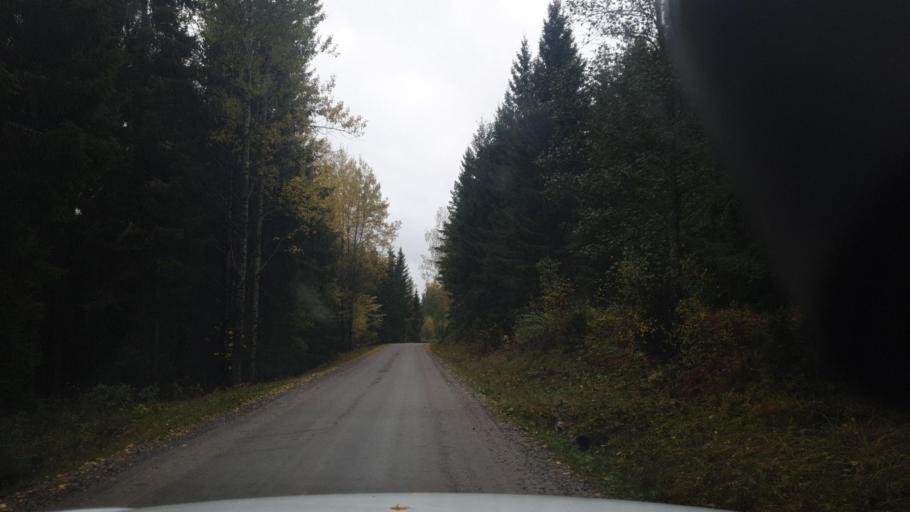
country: SE
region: Vaermland
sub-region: Karlstads Kommun
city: Edsvalla
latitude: 59.5008
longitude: 13.0303
